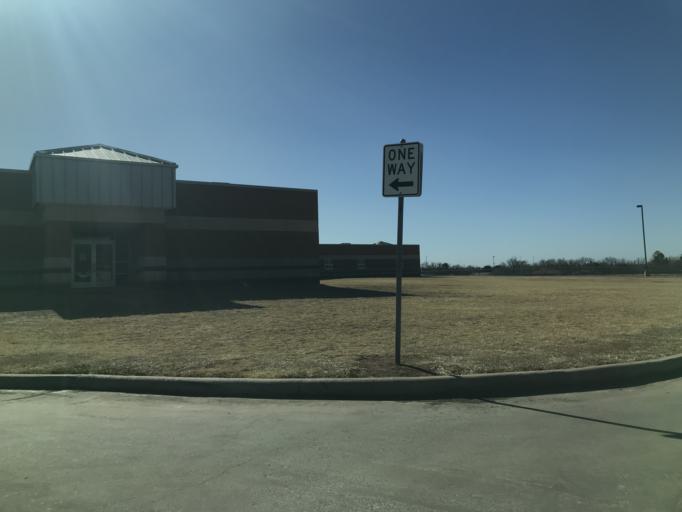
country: US
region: Texas
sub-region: Taylor County
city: Abilene
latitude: 32.4424
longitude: -99.7075
